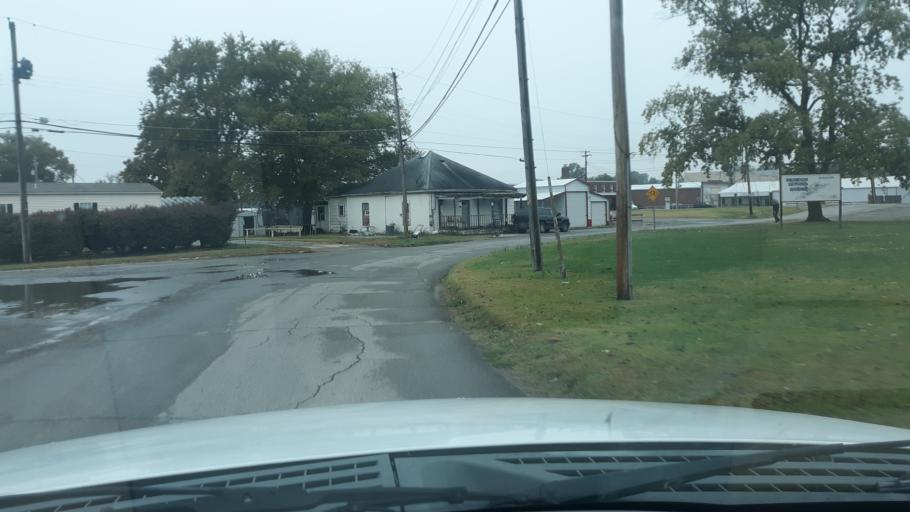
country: US
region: Illinois
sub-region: Saline County
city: Eldorado
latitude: 37.8126
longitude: -88.4355
